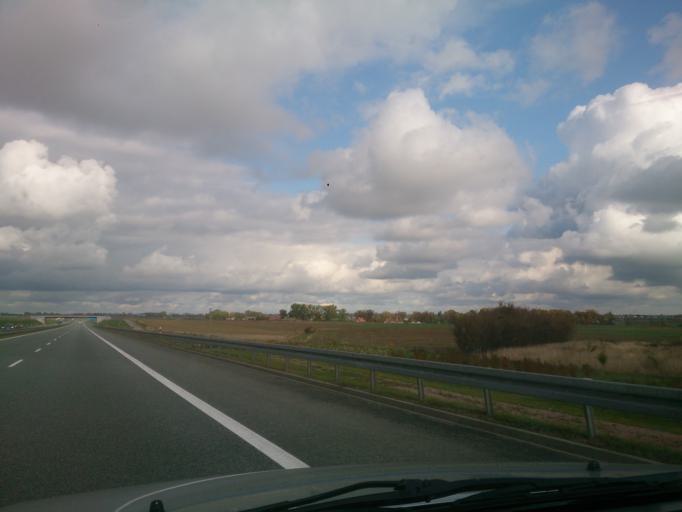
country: PL
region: Pomeranian Voivodeship
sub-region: Powiat gdanski
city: Pszczolki
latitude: 54.0872
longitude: 18.6919
